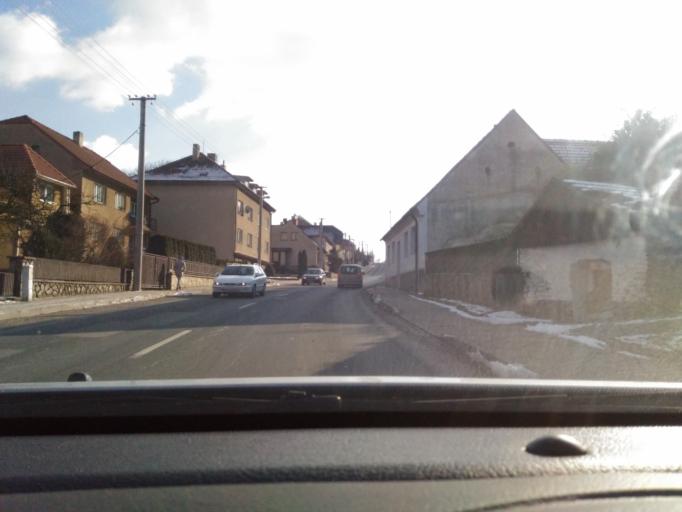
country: CZ
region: South Moravian
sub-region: Okres Brno-Venkov
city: Nedvedice
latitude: 49.4219
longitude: 16.3527
